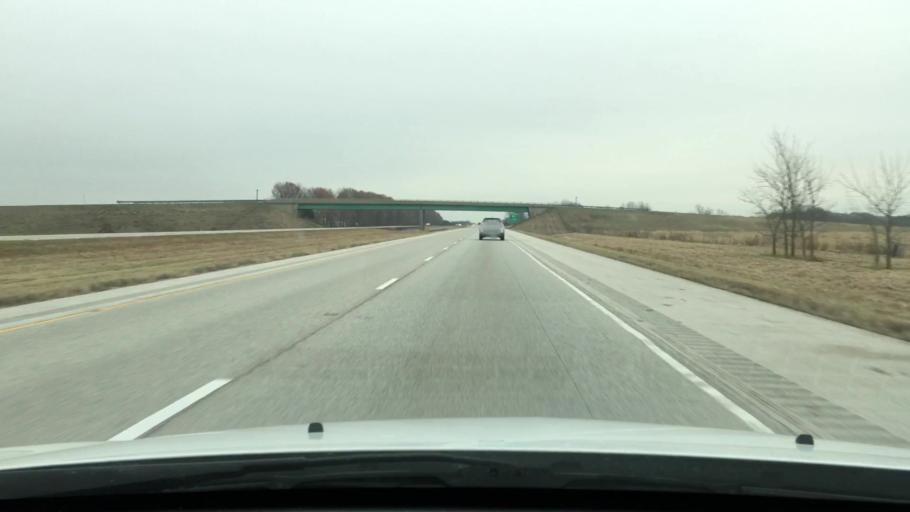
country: US
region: Illinois
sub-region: Morgan County
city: South Jacksonville
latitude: 39.6802
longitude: -90.3288
